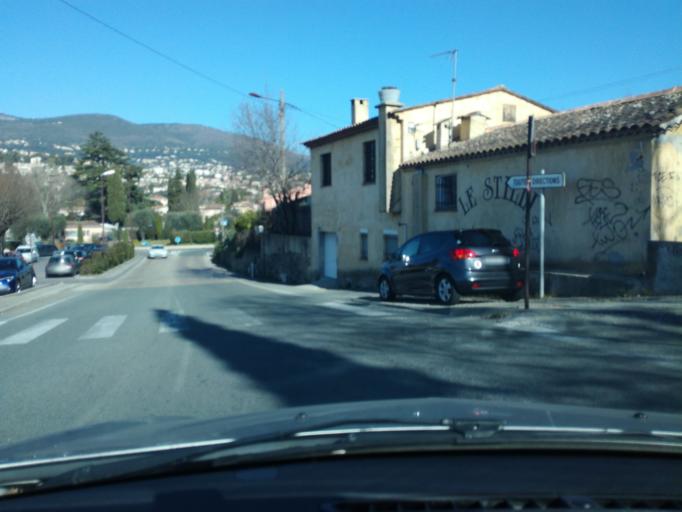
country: FR
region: Provence-Alpes-Cote d'Azur
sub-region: Departement des Alpes-Maritimes
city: Grasse
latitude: 43.6364
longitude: 6.9333
